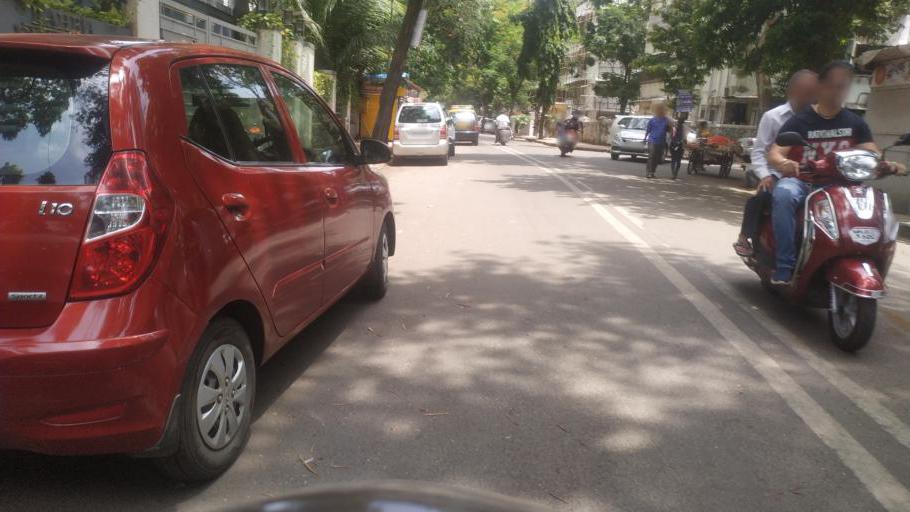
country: IN
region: Maharashtra
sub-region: Mumbai Suburban
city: Mumbai
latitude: 19.0182
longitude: 72.8335
